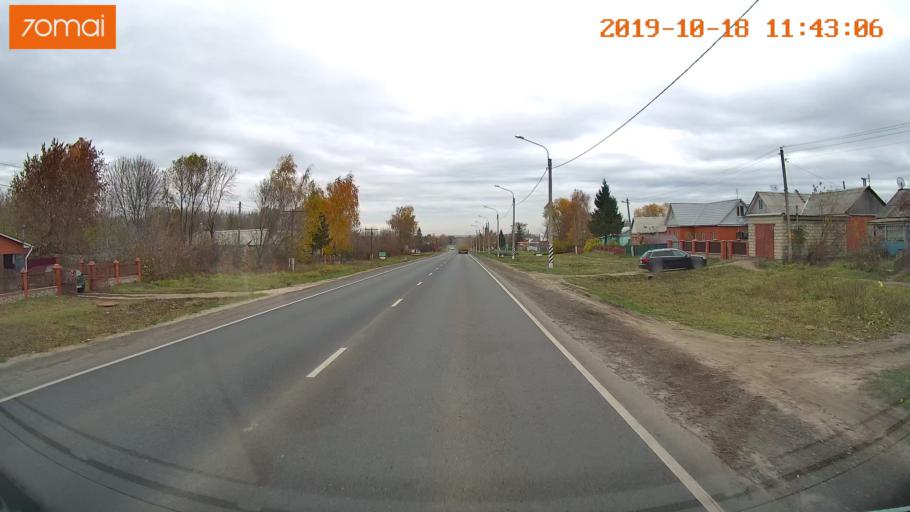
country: RU
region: Rjazan
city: Oktyabr'skiy
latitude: 54.1940
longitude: 38.9387
